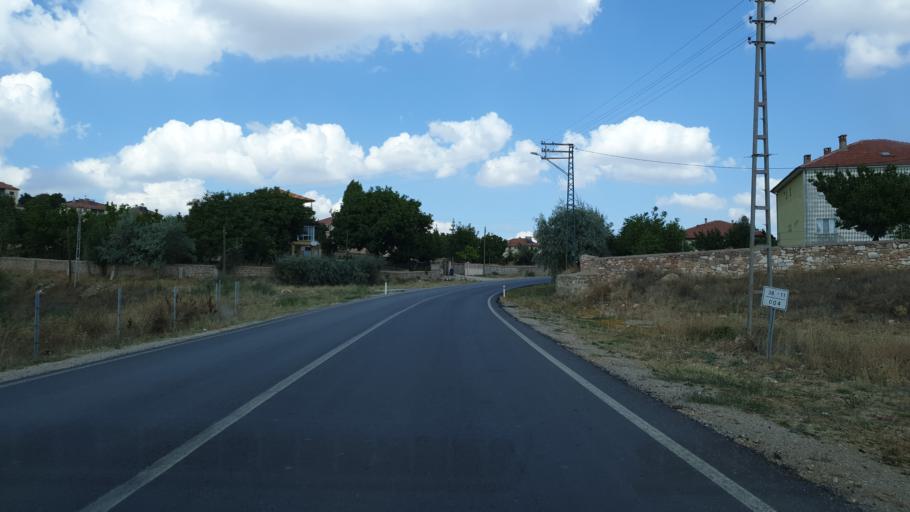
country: TR
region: Kayseri
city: Felahiye
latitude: 39.1080
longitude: 35.6003
